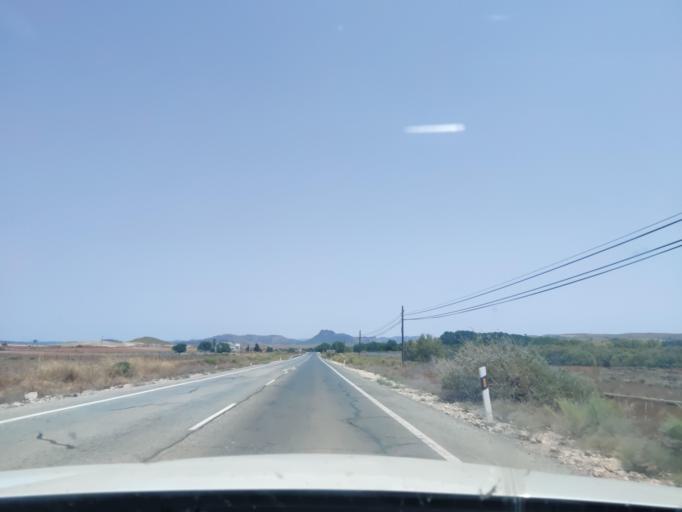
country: ES
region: Castille-La Mancha
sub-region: Provincia de Albacete
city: Hellin
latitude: 38.4968
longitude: -1.6544
